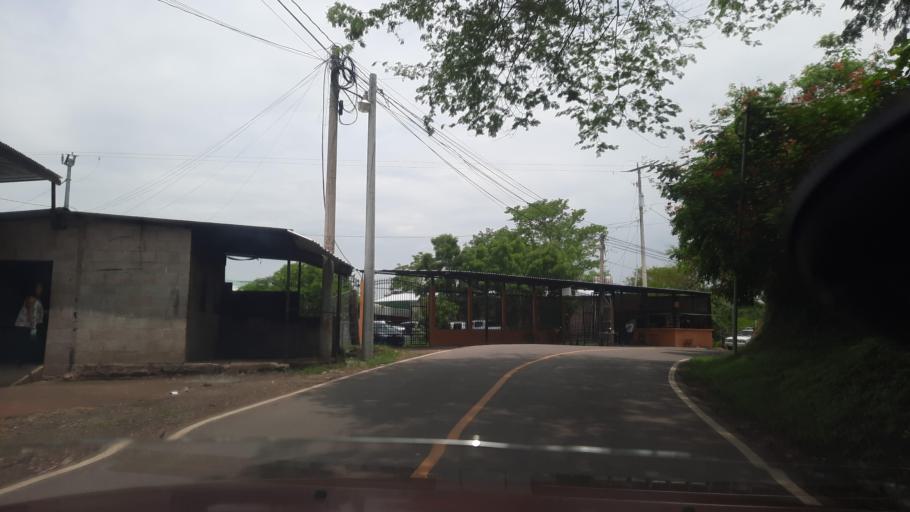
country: SV
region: La Union
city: Santa Rosa de Lima
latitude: 13.6483
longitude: -87.8477
